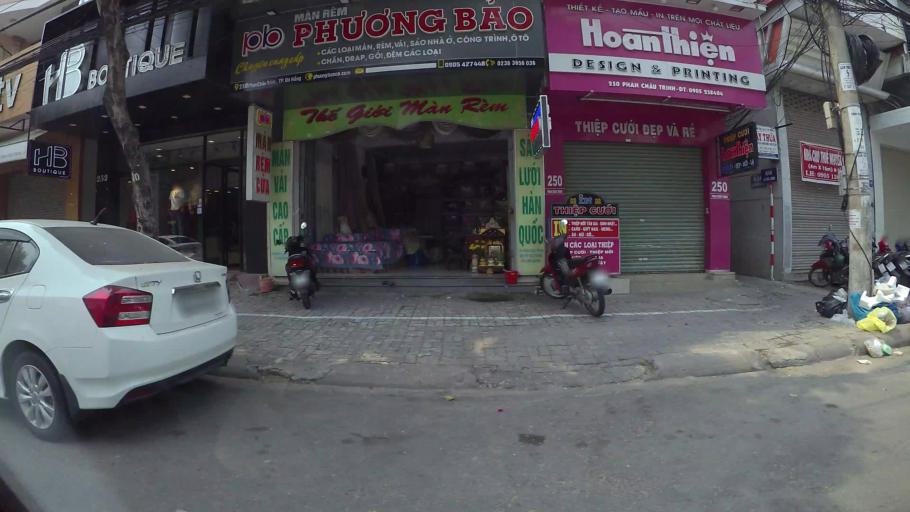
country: VN
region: Da Nang
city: Da Nang
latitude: 16.0597
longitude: 108.2195
